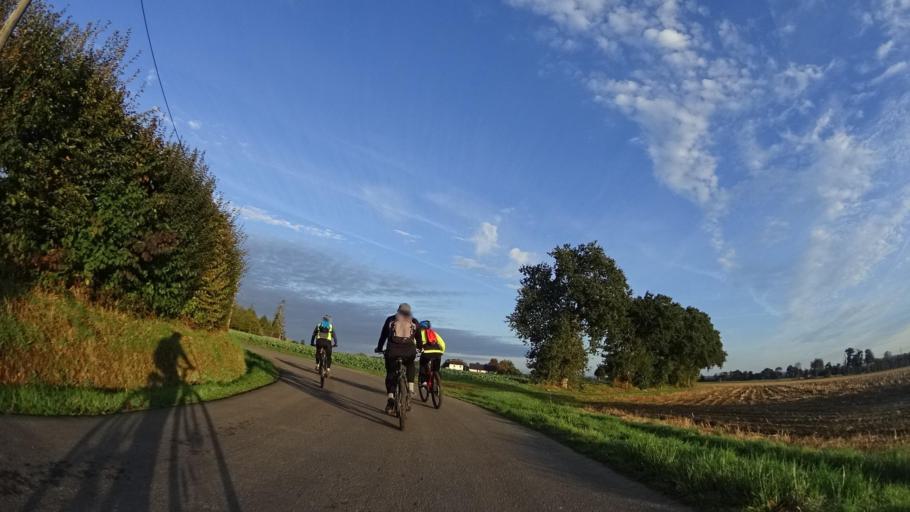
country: FR
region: Brittany
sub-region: Departement des Cotes-d'Armor
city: Evran
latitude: 48.3552
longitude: -1.9432
